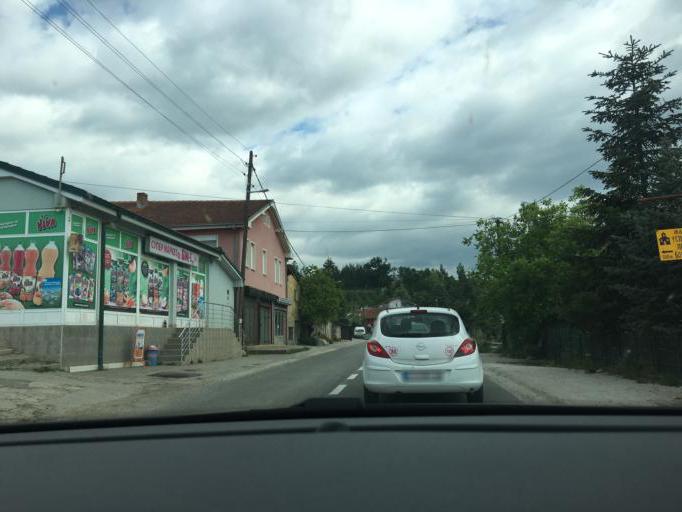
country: MK
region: Resen
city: Jankovec
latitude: 41.1108
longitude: 21.0117
